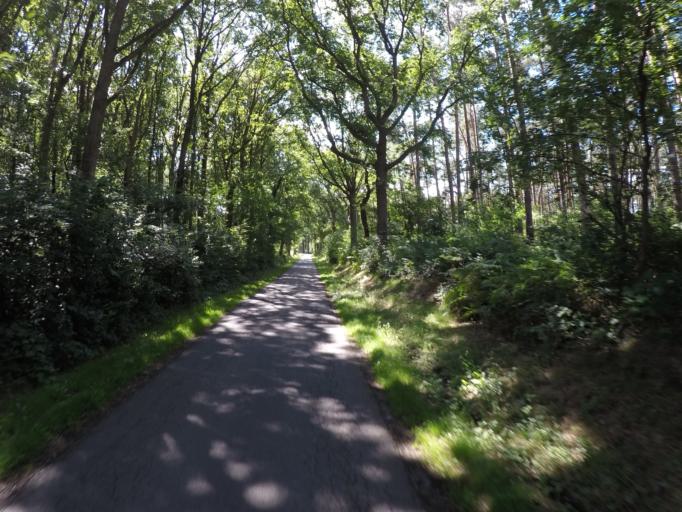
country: BE
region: Flanders
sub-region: Provincie Antwerpen
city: Herenthout
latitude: 51.1260
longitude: 4.7294
